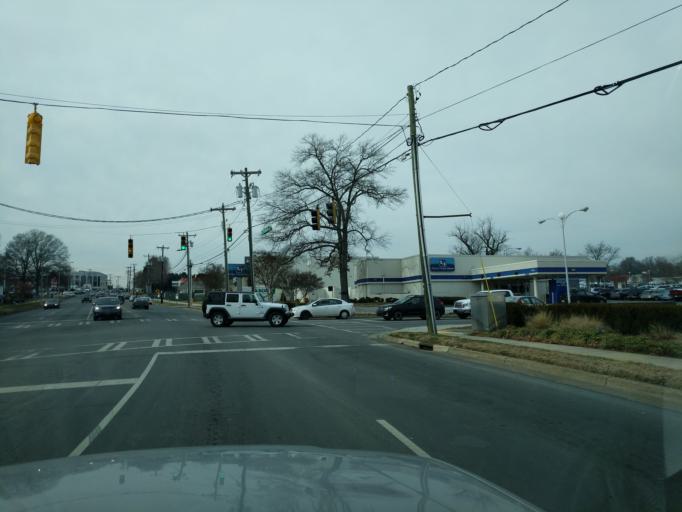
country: US
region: North Carolina
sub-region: Mecklenburg County
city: Charlotte
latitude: 35.1720
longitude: -80.8468
